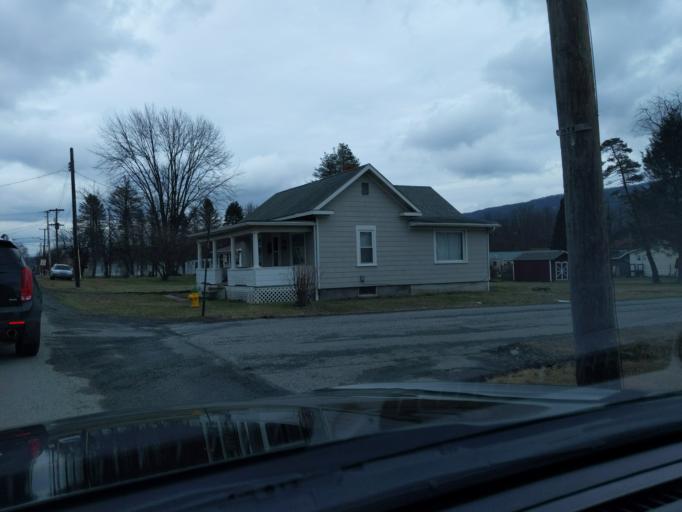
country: US
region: Pennsylvania
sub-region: Blair County
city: Bellwood
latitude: 40.6046
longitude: -78.3331
